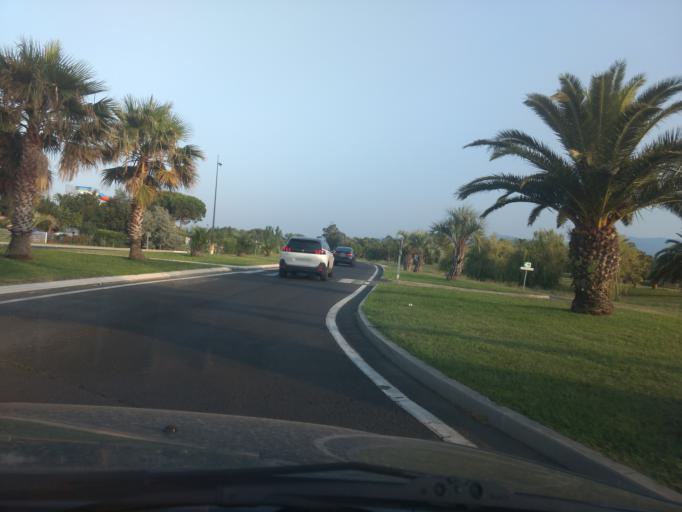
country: FR
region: Languedoc-Roussillon
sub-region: Departement des Pyrenees-Orientales
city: Saint-Cyprien-Plage
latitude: 42.6246
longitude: 3.0225
